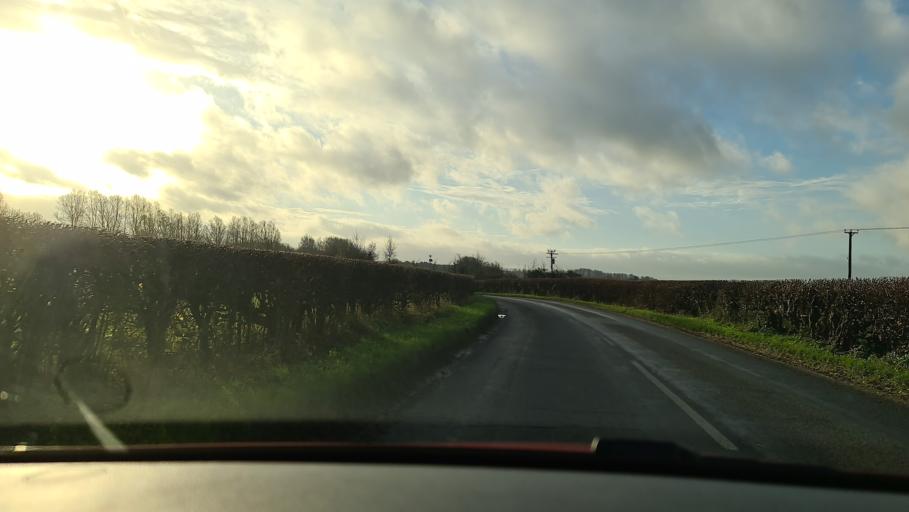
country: GB
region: England
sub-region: Buckinghamshire
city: Haddenham
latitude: 51.7971
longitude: -0.9480
